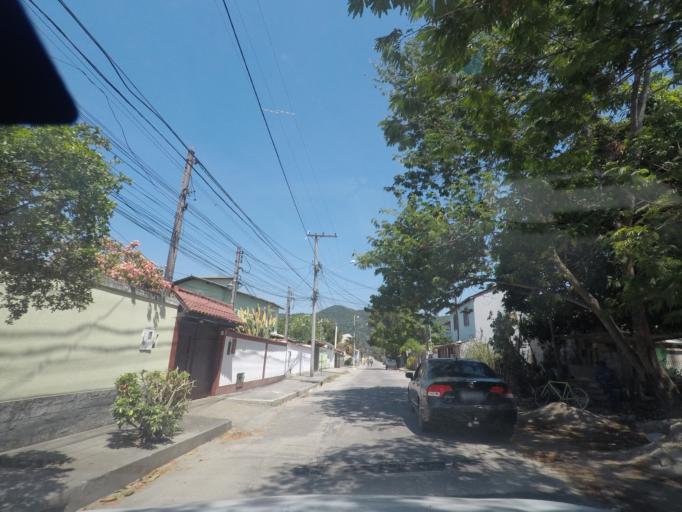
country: BR
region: Rio de Janeiro
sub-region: Niteroi
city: Niteroi
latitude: -22.9384
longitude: -43.0229
